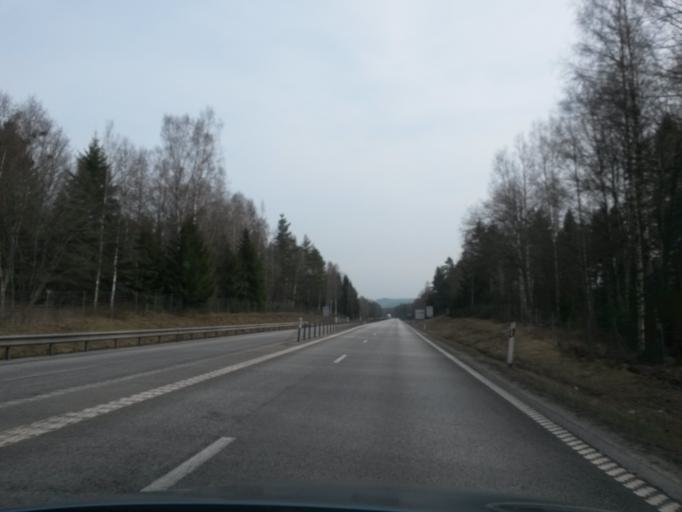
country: SE
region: Vaestra Goetaland
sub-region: Gullspangs Kommun
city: Anderstorp
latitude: 58.9173
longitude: 14.3917
